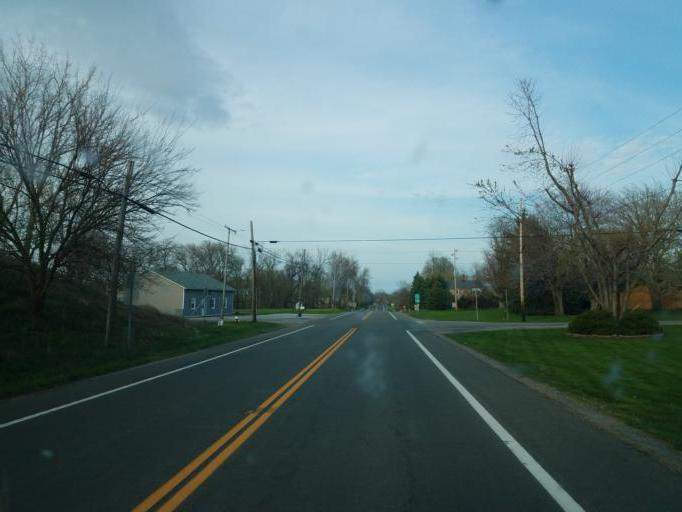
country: US
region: Ohio
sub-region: Lorain County
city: Vermilion
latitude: 41.3889
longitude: -82.4463
